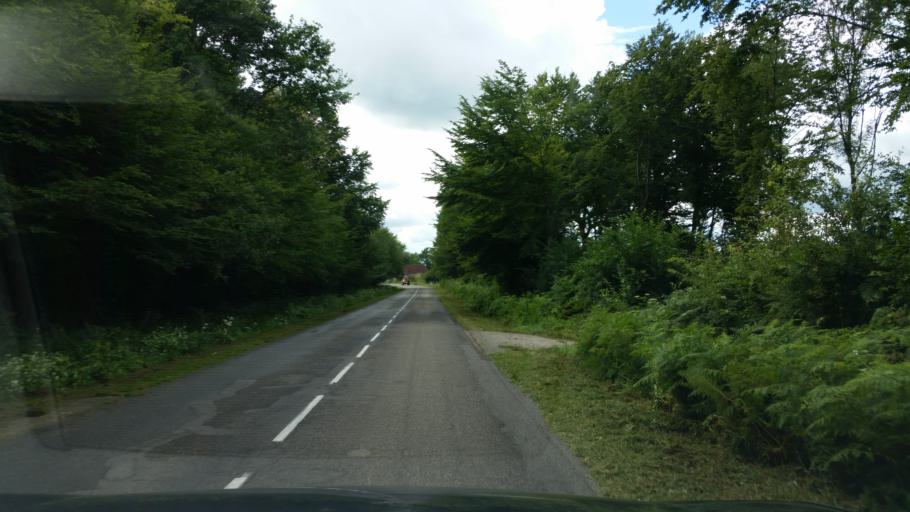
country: FR
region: Bourgogne
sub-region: Departement de Saone-et-Loire
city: Saint-Usuge
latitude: 46.7015
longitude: 5.3499
